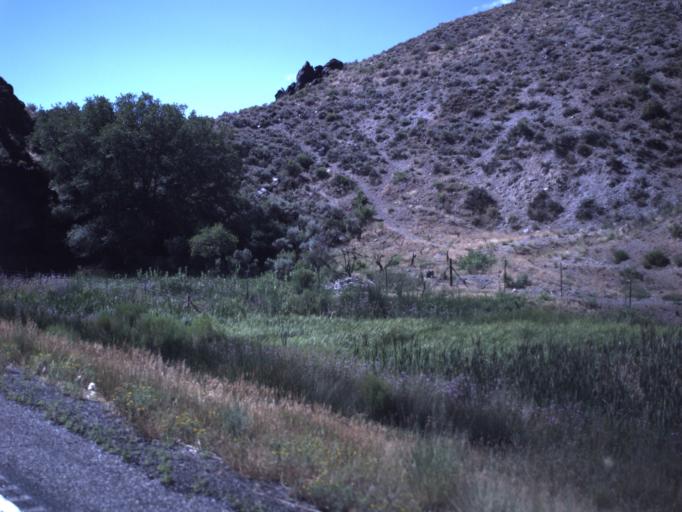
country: US
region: Utah
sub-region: Sevier County
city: Monroe
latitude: 38.4785
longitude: -112.2415
